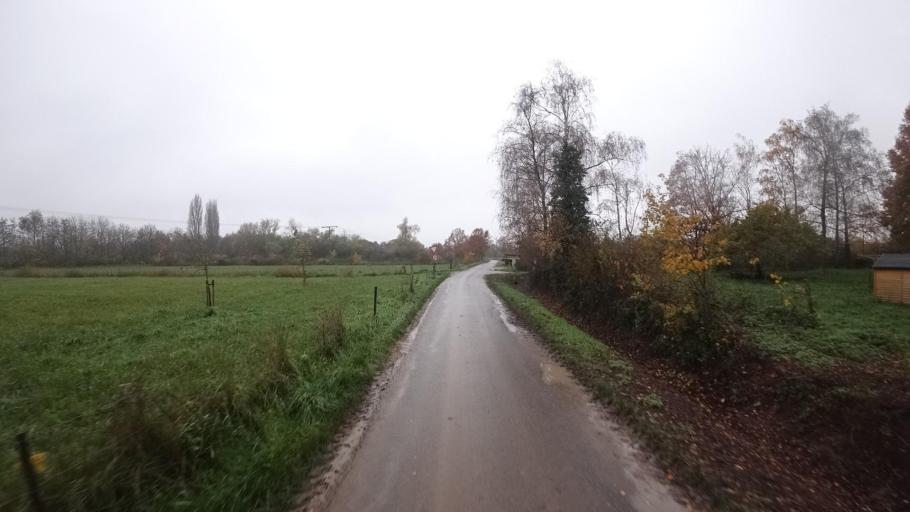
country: DE
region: Rheinland-Pfalz
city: Gimbsheim
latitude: 49.7780
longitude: 8.3881
